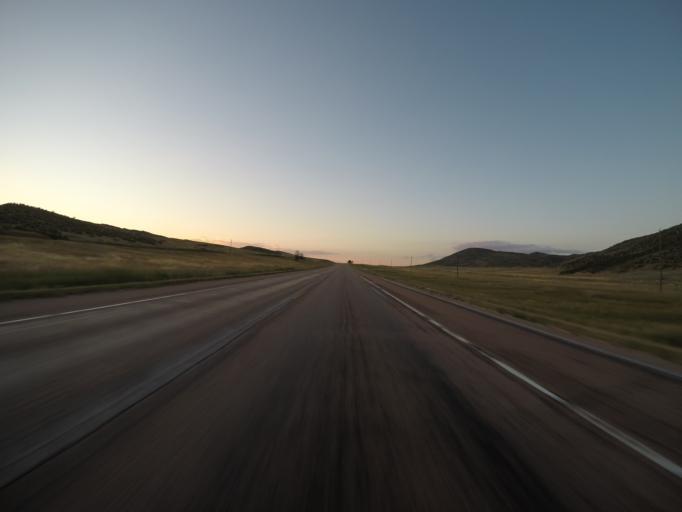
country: US
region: Colorado
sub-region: Larimer County
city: Laporte
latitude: 40.7380
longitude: -105.1709
